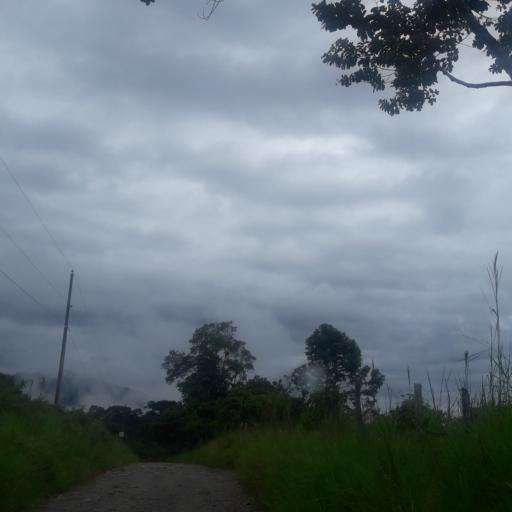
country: EC
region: Napo
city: Archidona
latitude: -0.9184
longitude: -77.8197
